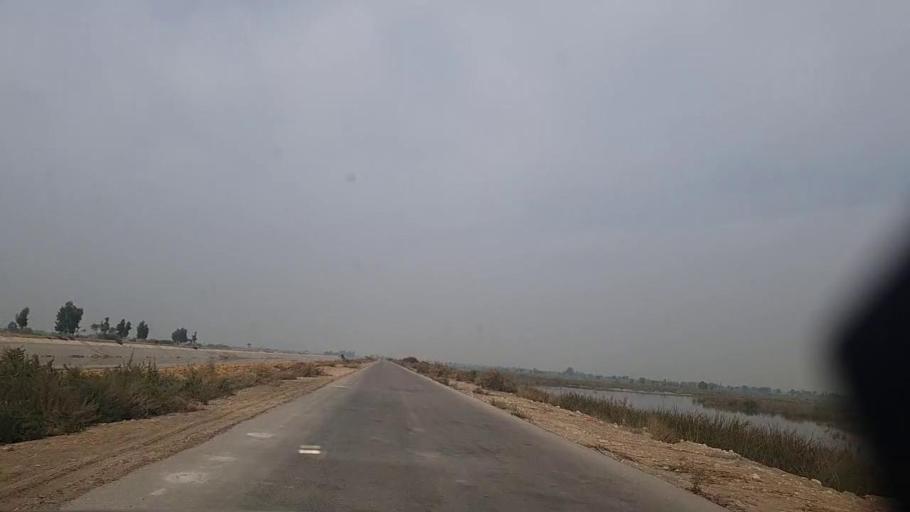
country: PK
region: Sindh
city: Sakrand
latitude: 26.2697
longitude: 68.2360
